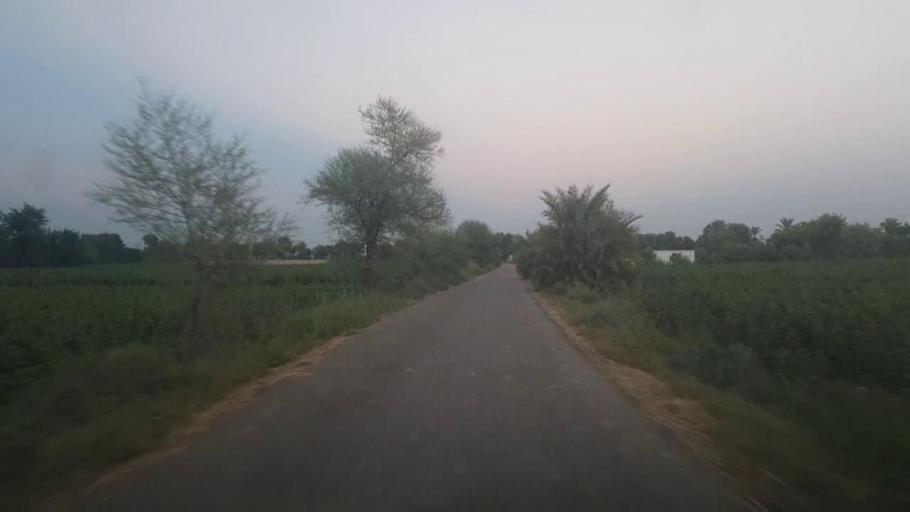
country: PK
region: Sindh
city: Ubauro
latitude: 28.1058
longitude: 69.7774
